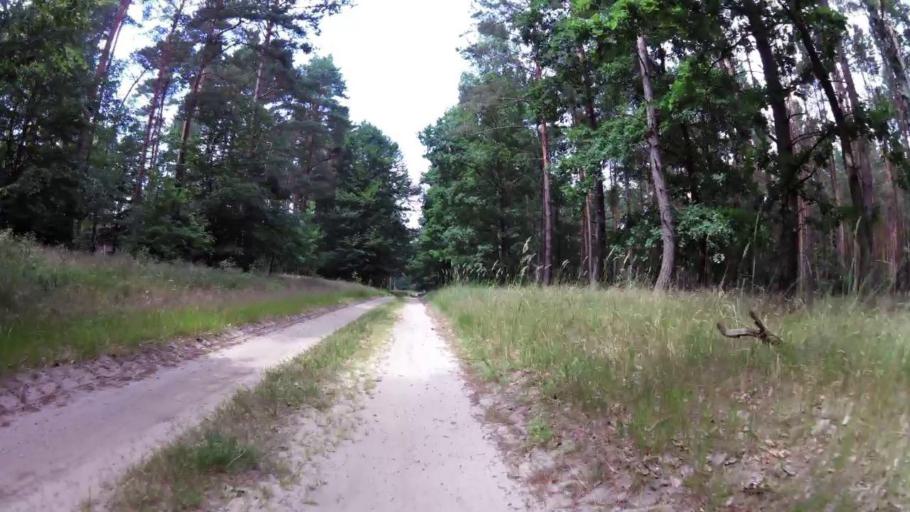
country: PL
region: West Pomeranian Voivodeship
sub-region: Powiat lobeski
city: Lobez
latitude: 53.5564
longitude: 15.6710
